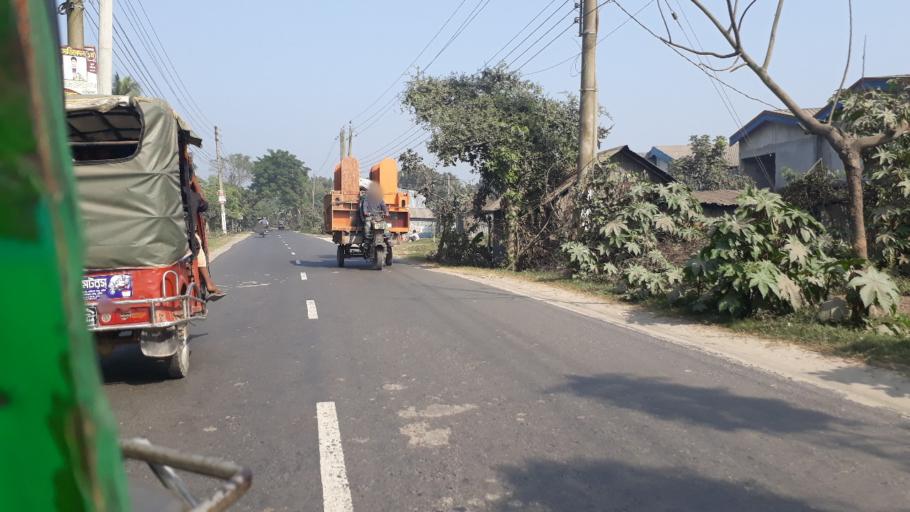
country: BD
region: Khulna
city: Kushtia
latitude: 23.8780
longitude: 89.0853
